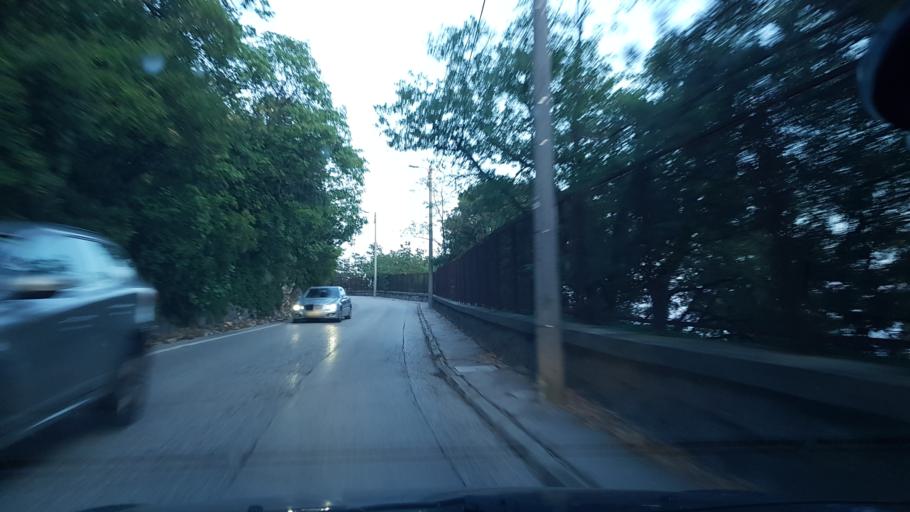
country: IT
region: Friuli Venezia Giulia
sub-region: Provincia di Trieste
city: Villa Opicina
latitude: 45.6799
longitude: 13.7762
